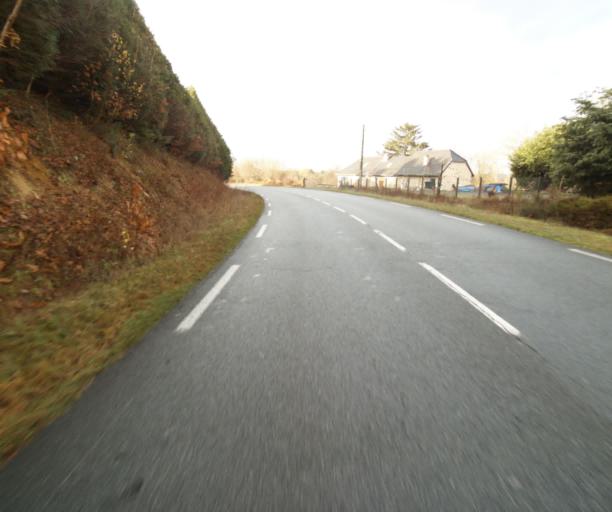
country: FR
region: Limousin
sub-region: Departement de la Correze
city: Saint-Mexant
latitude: 45.2624
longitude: 1.6371
